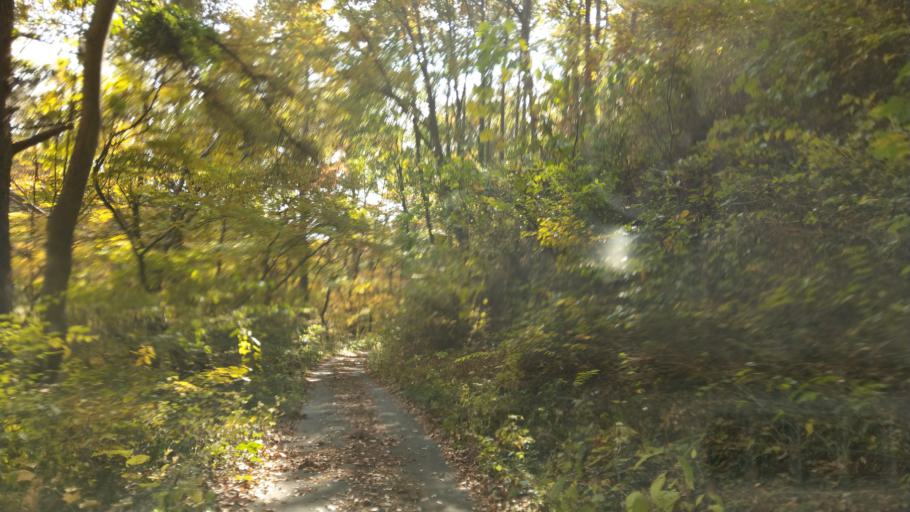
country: JP
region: Nagano
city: Komoro
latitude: 36.3660
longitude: 138.4410
